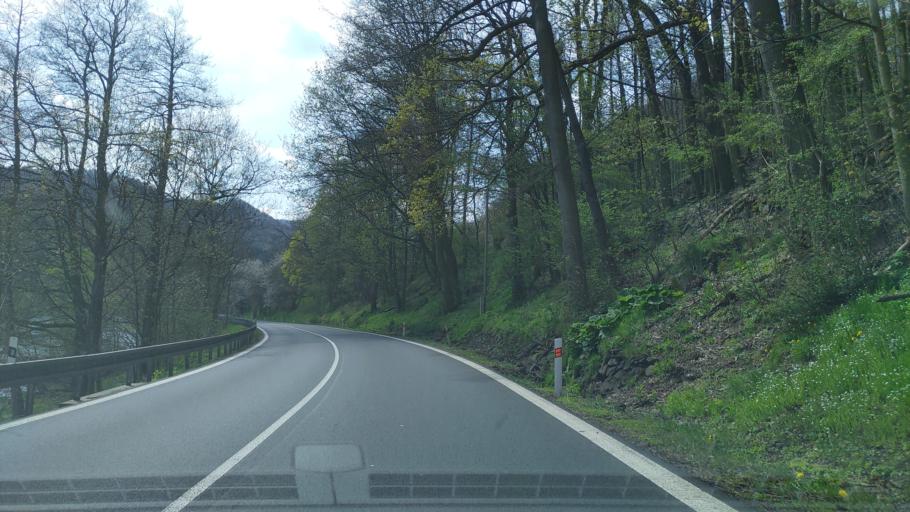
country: CZ
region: Ustecky
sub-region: Okres Chomutov
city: Perstejn
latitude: 50.3562
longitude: 13.0742
